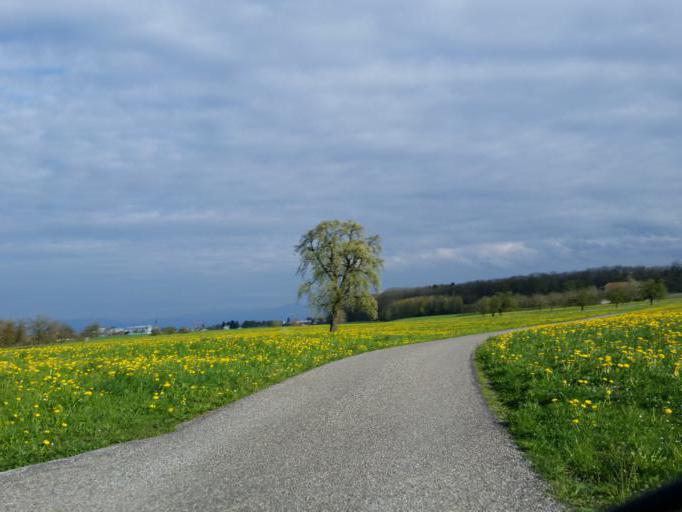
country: CH
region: Thurgau
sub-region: Arbon District
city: Uttwil
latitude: 47.5770
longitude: 9.3436
